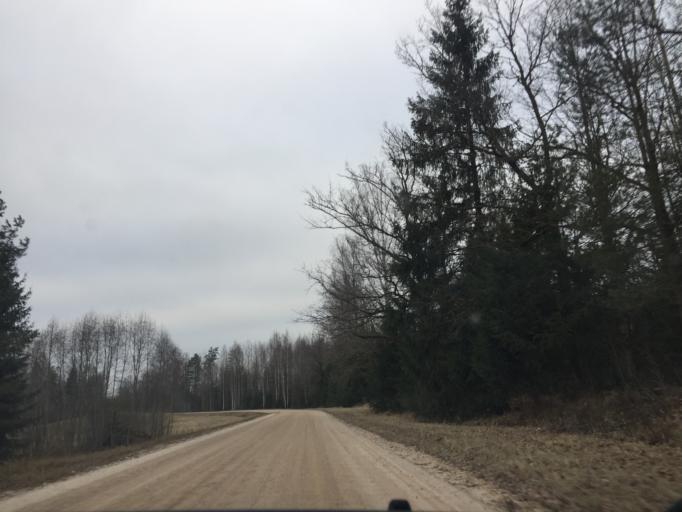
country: LV
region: Ligatne
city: Ligatne
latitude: 57.2147
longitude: 25.1310
